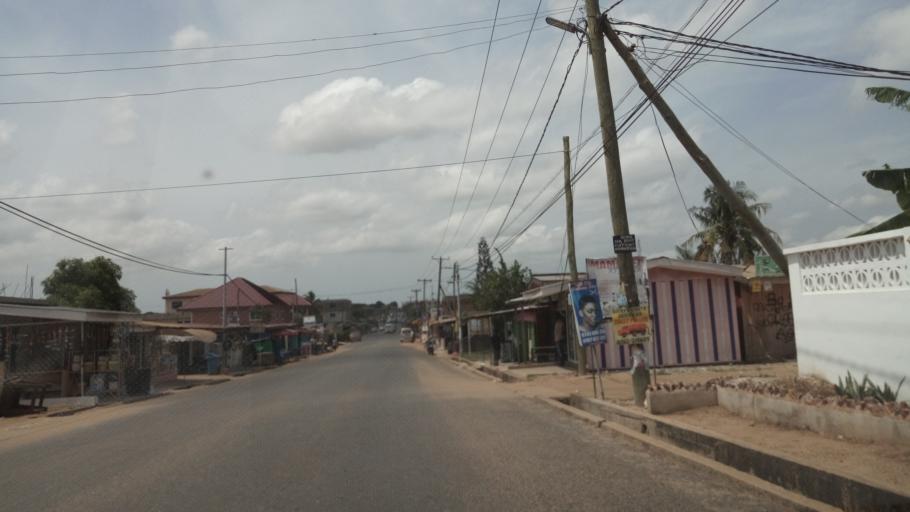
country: GH
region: Greater Accra
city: Medina Estates
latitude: 5.6840
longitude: -0.1605
